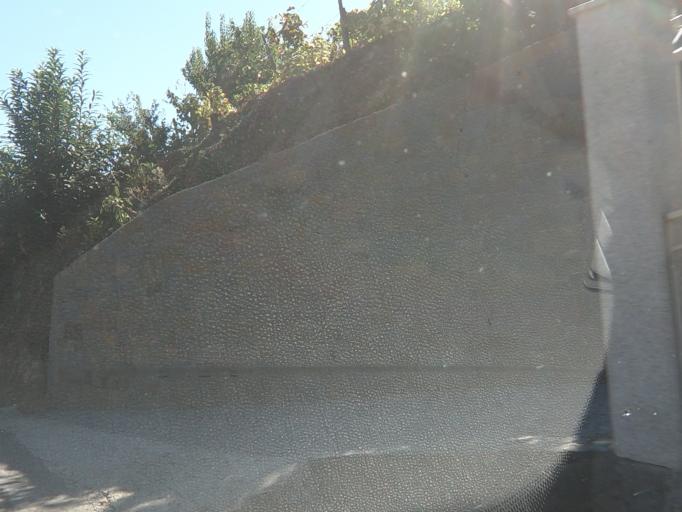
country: PT
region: Vila Real
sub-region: Santa Marta de Penaguiao
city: Santa Marta de Penaguiao
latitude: 41.2273
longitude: -7.7883
